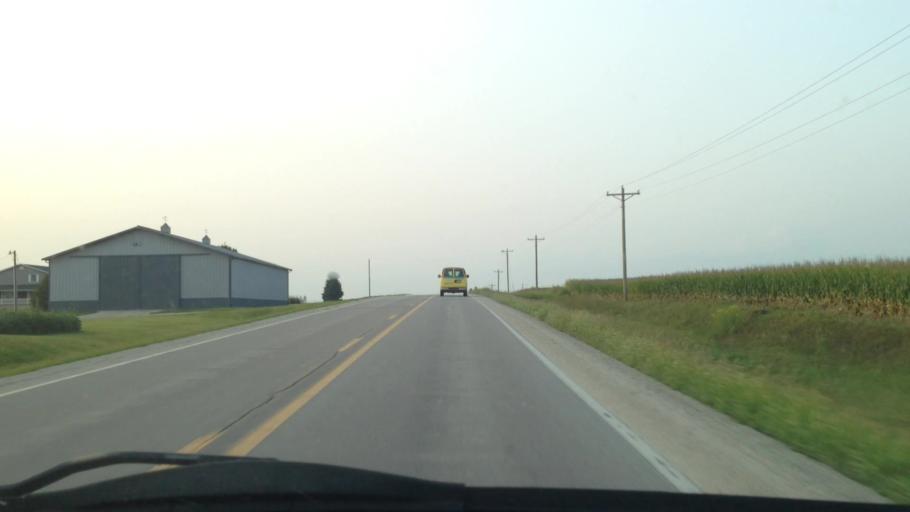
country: US
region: Iowa
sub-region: Benton County
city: Atkins
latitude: 42.0428
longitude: -91.8693
